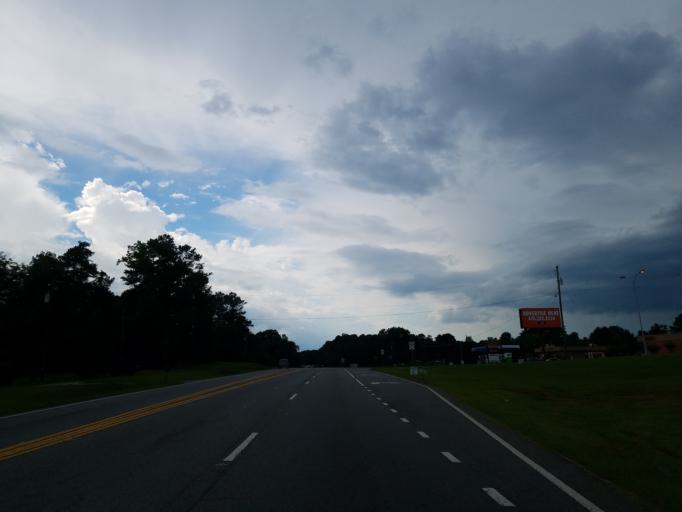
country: US
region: Georgia
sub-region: Bartow County
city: Adairsville
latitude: 34.3433
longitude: -84.9093
